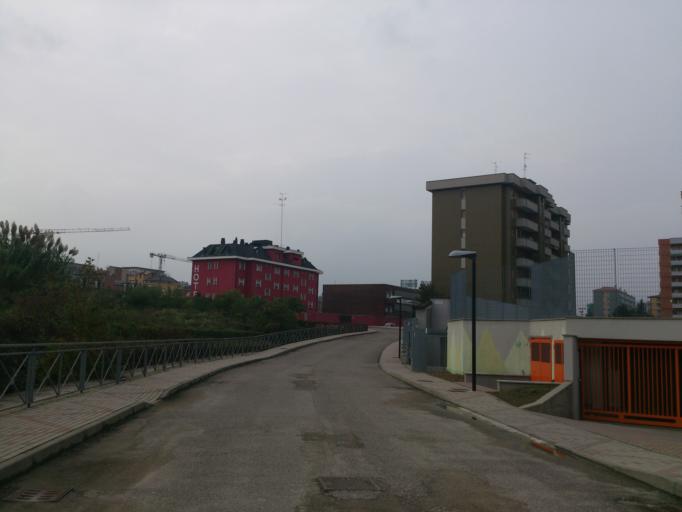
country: IT
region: Lombardy
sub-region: Citta metropolitana di Milano
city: Civesio
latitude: 45.4078
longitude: 9.2725
